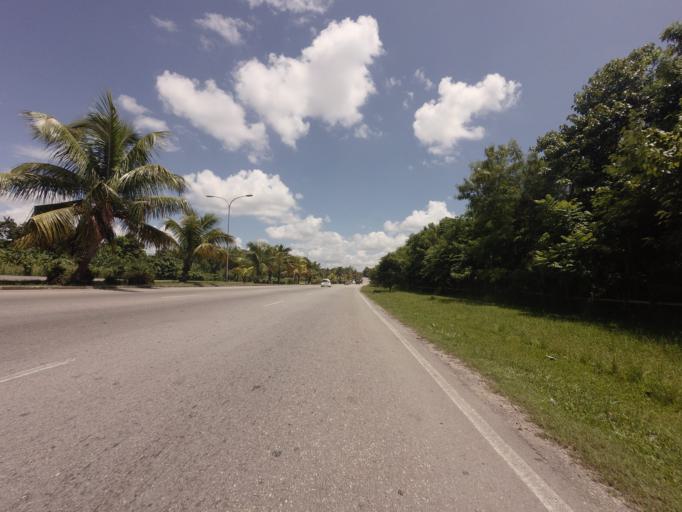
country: CU
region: La Habana
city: Arroyo Naranjo
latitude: 23.0445
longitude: -82.3710
